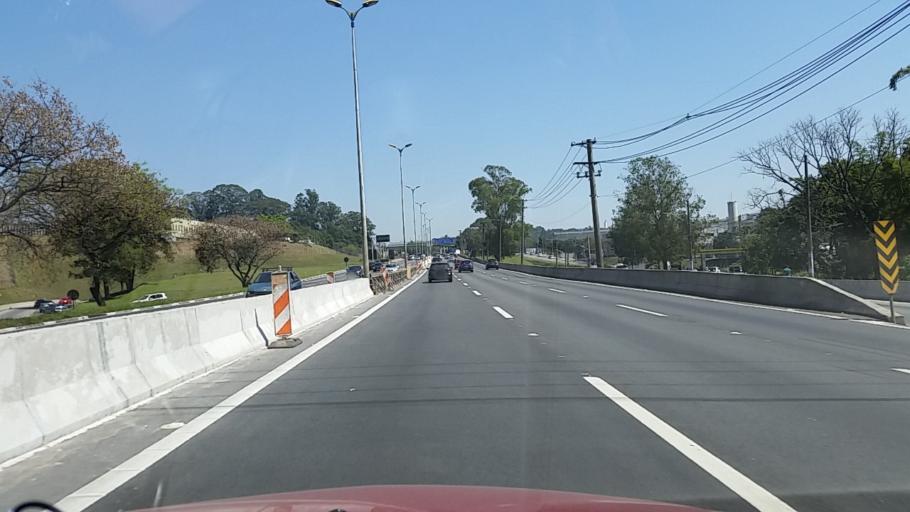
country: BR
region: Sao Paulo
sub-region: Taboao Da Serra
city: Taboao da Serra
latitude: -23.5837
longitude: -46.7812
